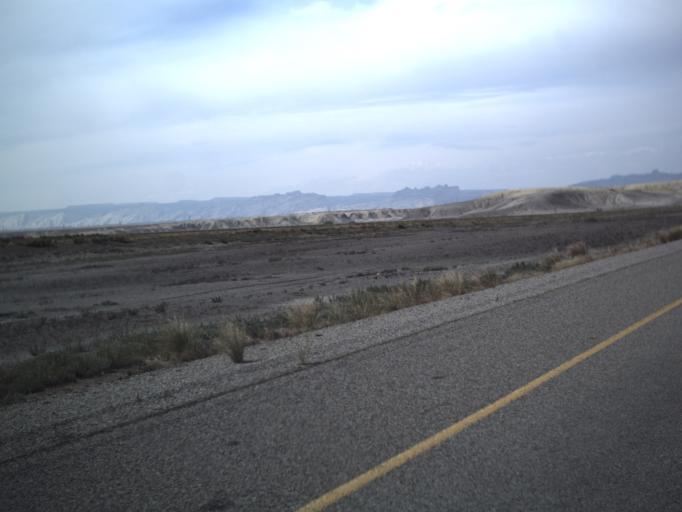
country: US
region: Utah
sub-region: Carbon County
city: East Carbon City
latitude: 38.9837
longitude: -110.2337
